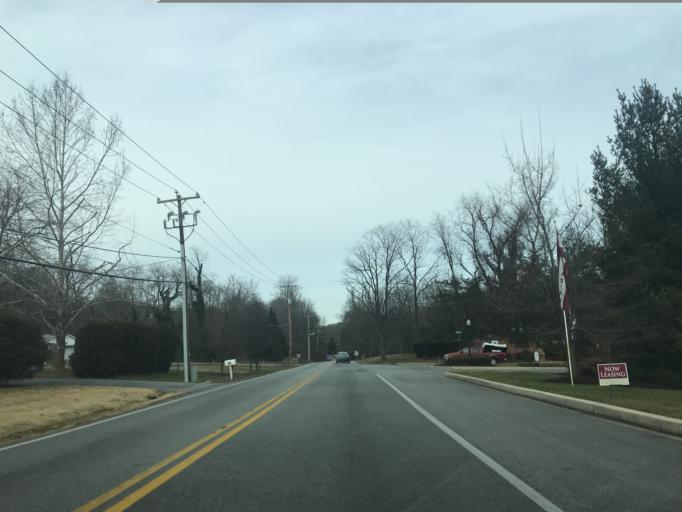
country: US
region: Maryland
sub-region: Cecil County
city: Elkton
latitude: 39.6162
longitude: -75.7919
